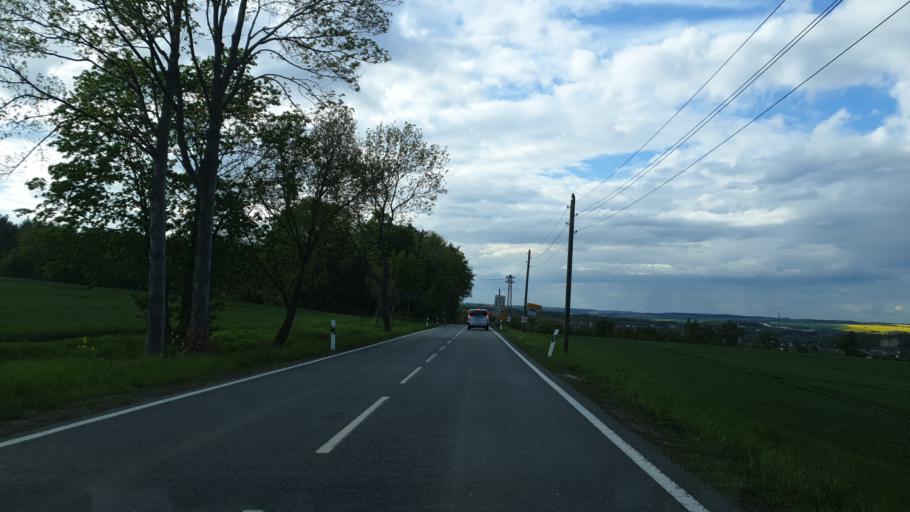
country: DE
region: Saxony
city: Lichtenstein
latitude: 50.7336
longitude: 12.6371
